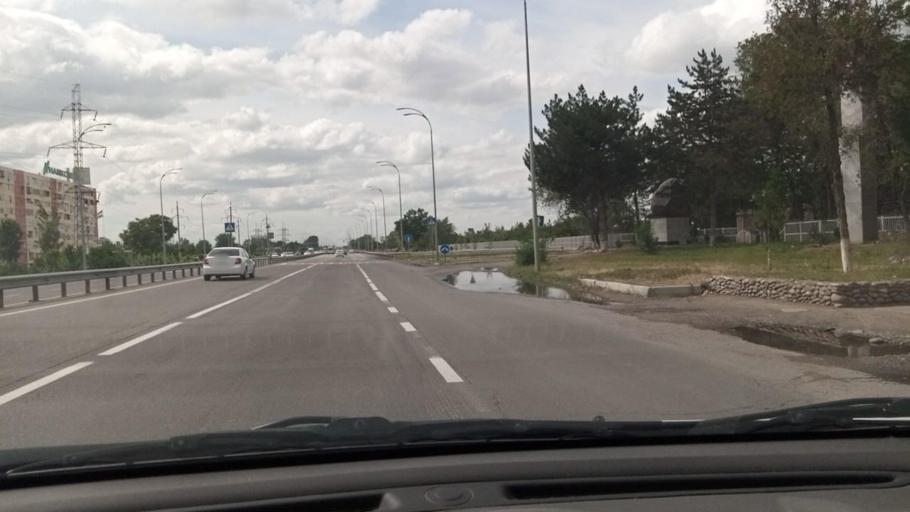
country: UZ
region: Toshkent Shahri
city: Bektemir
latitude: 41.2551
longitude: 69.3829
